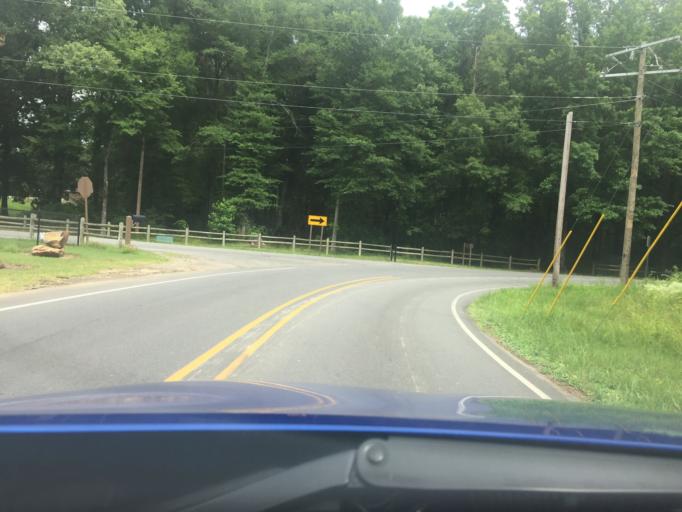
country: US
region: Arkansas
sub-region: Pulaski County
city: Maumelle
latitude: 34.8297
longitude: -92.4362
